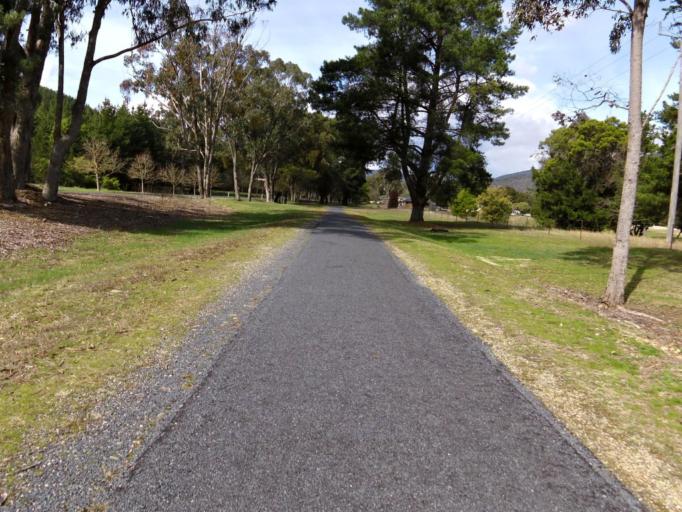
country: AU
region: Victoria
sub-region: Alpine
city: Mount Beauty
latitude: -36.7130
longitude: 146.9388
